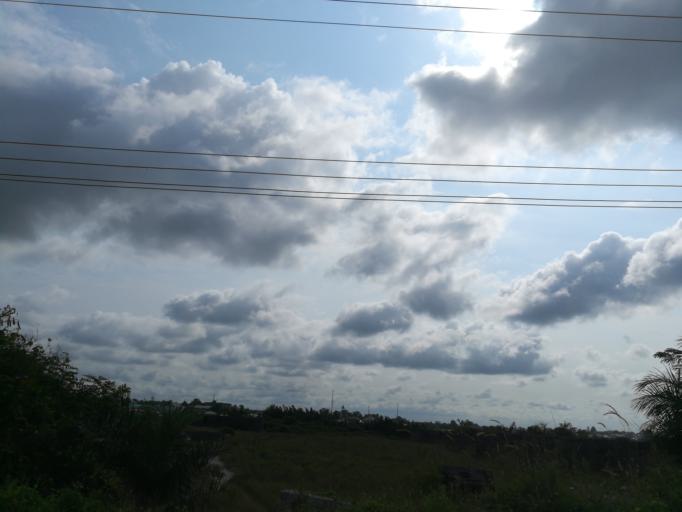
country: NG
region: Rivers
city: Okrika
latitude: 4.7516
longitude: 7.0845
